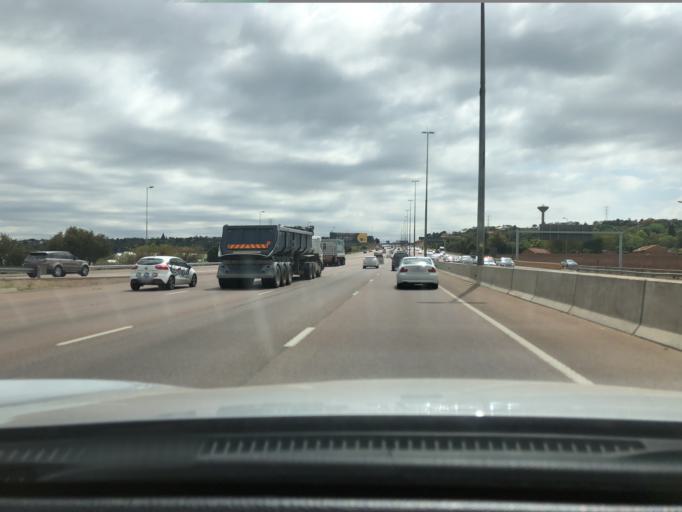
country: ZA
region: Gauteng
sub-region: City of Tshwane Metropolitan Municipality
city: Centurion
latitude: -25.8274
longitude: 28.2455
